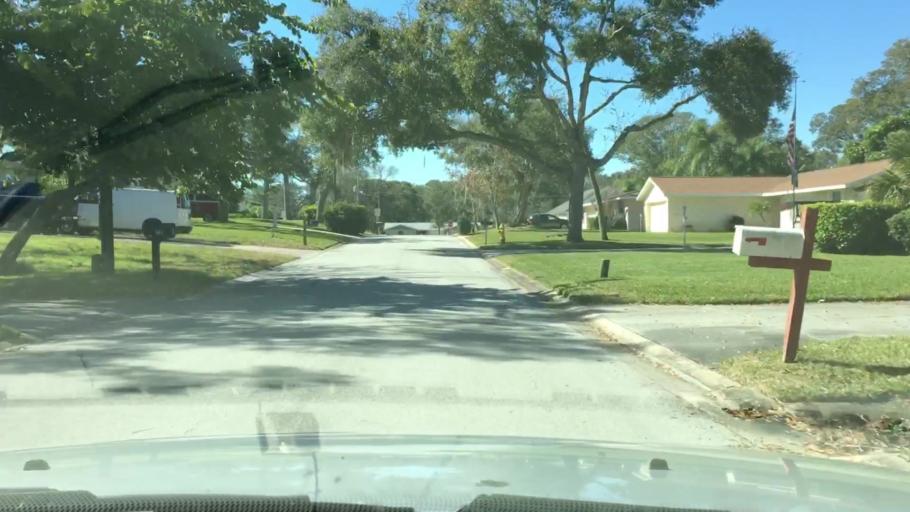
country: US
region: Florida
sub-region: Volusia County
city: Ormond Beach
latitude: 29.3019
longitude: -81.0661
